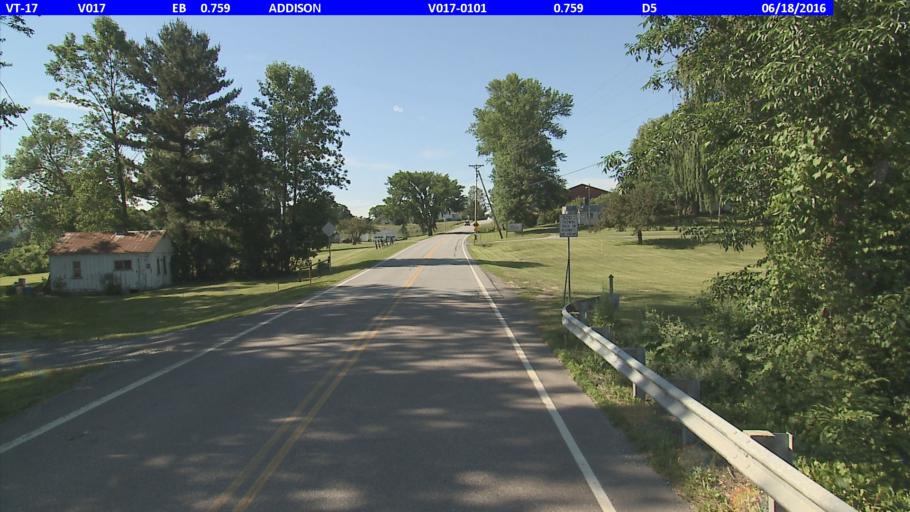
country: US
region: New York
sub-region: Essex County
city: Port Henry
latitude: 44.0414
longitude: -73.4156
